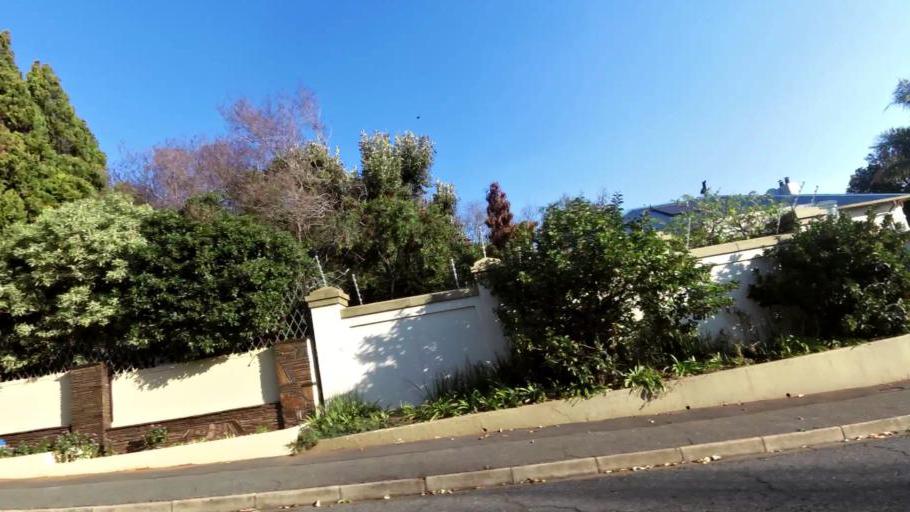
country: ZA
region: Gauteng
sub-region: City of Johannesburg Metropolitan Municipality
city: Johannesburg
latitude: -26.1895
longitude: 27.9980
